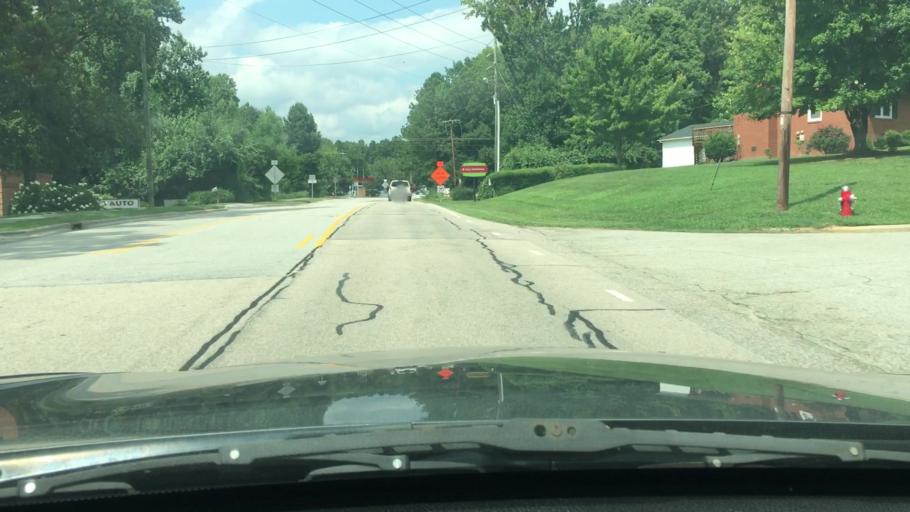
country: US
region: North Carolina
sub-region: Wake County
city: Cary
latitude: 35.7844
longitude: -78.7921
